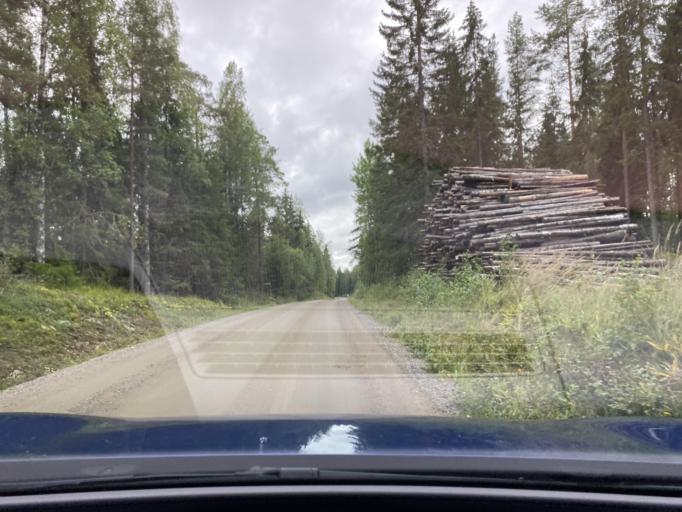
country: FI
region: Pirkanmaa
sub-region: Lounais-Pirkanmaa
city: Punkalaidun
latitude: 61.1961
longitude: 23.1814
